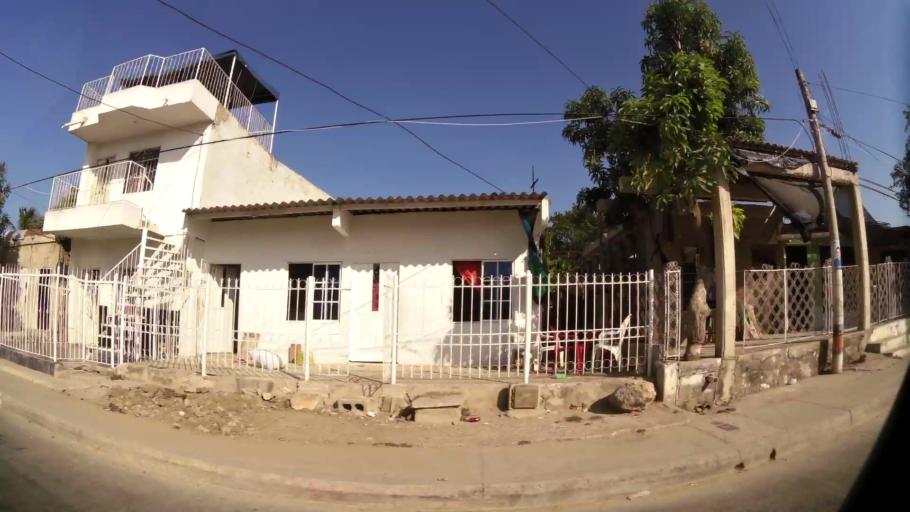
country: CO
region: Bolivar
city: Cartagena
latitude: 10.4130
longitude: -75.4998
